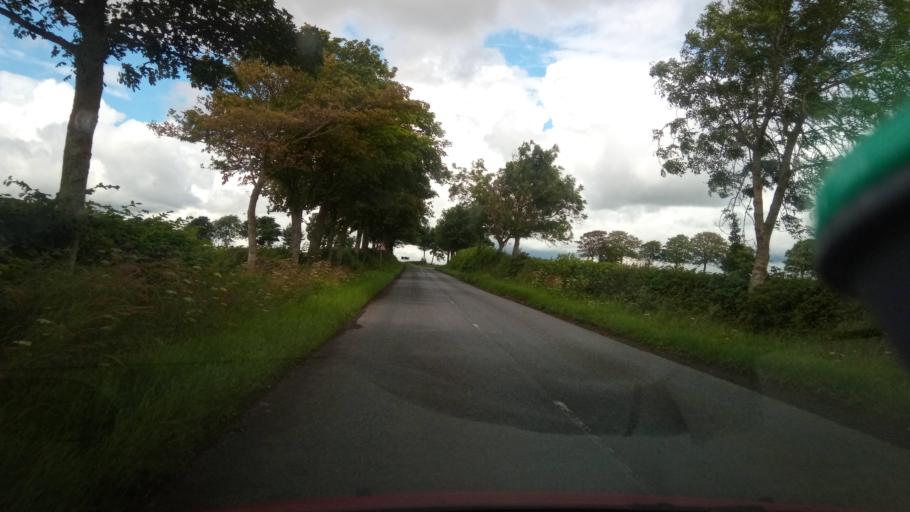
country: GB
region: Scotland
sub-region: The Scottish Borders
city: Kelso
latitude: 55.5823
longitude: -2.4235
